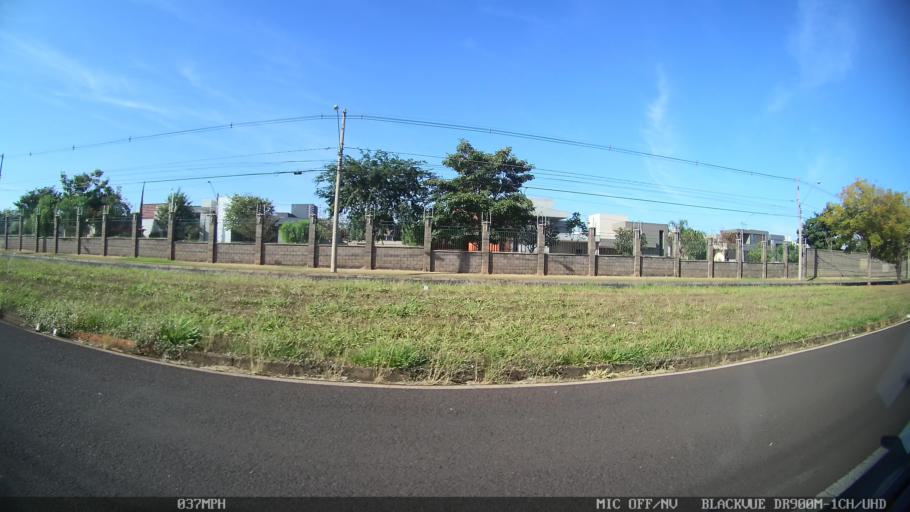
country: BR
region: Sao Paulo
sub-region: Sao Jose Do Rio Preto
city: Sao Jose do Rio Preto
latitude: -20.7759
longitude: -49.3396
